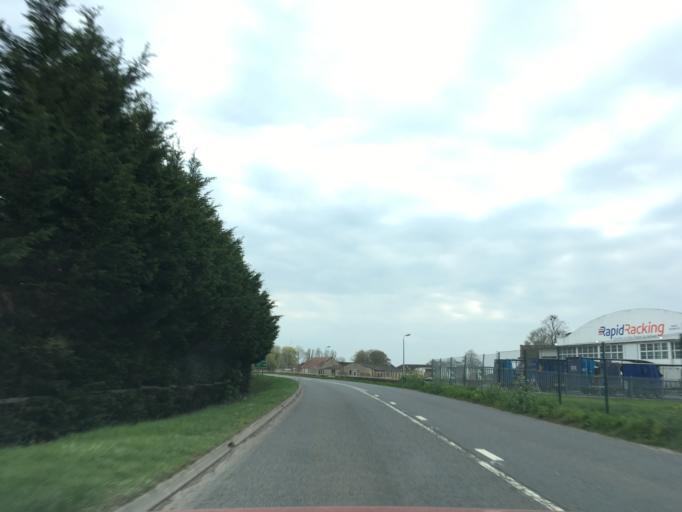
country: GB
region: England
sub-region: Gloucestershire
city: Coates
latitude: 51.6645
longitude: -2.0513
